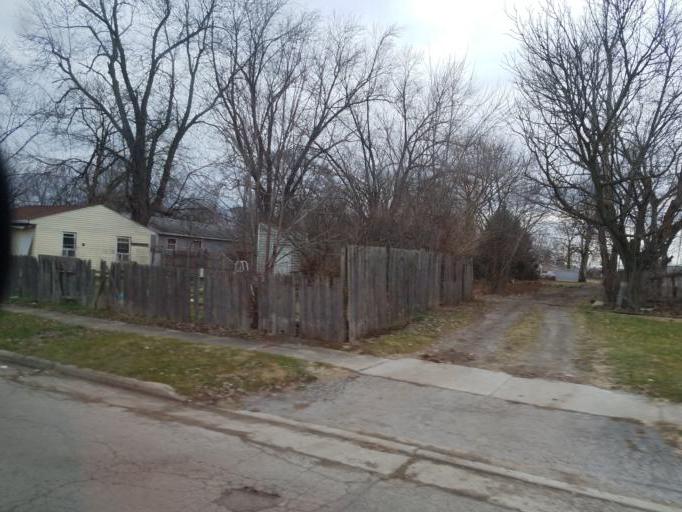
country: US
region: Ohio
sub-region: Marion County
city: Marion
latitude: 40.5983
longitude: -83.1141
